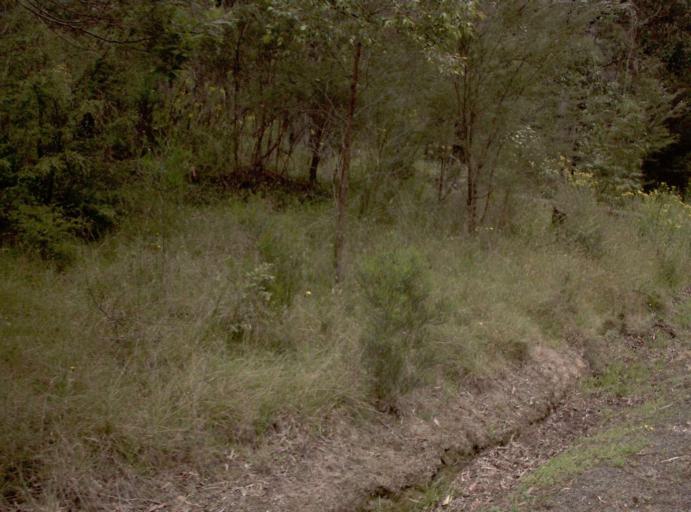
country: AU
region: New South Wales
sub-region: Bombala
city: Bombala
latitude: -37.3737
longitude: 149.2043
